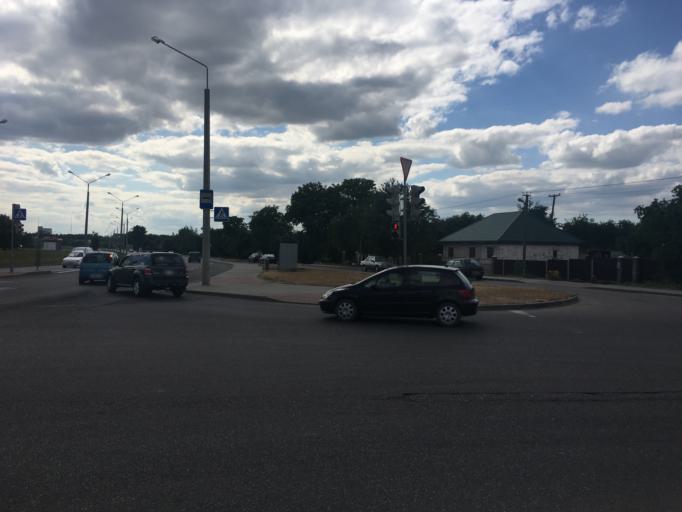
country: BY
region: Grodnenskaya
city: Hrodna
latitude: 53.7225
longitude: 23.8228
